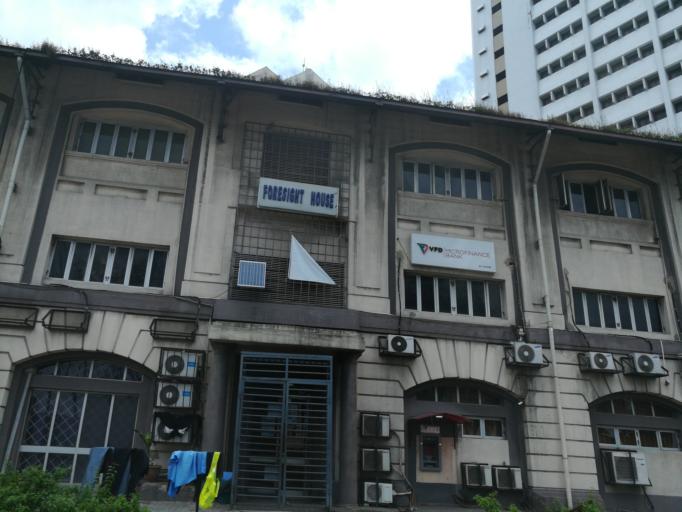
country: NG
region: Lagos
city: Lagos
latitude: 6.4575
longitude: 3.3800
